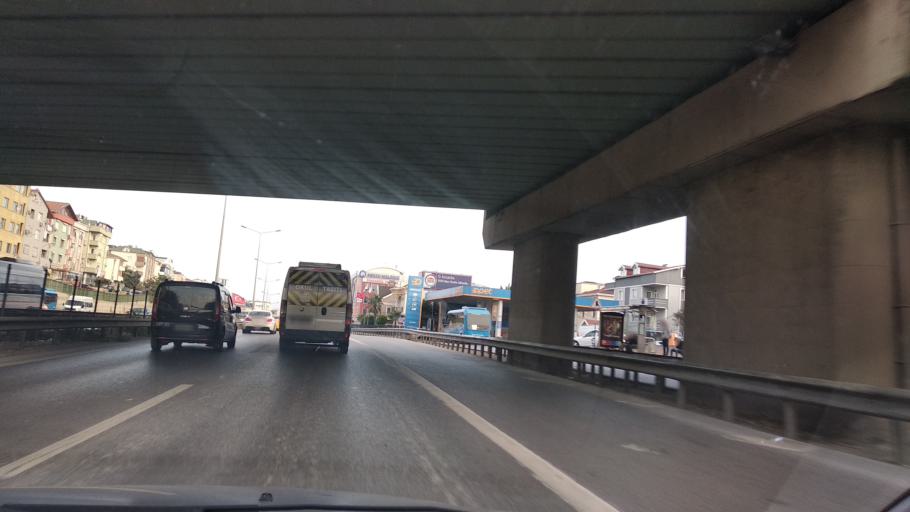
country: TR
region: Istanbul
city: Pendik
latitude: 40.8600
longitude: 29.2809
